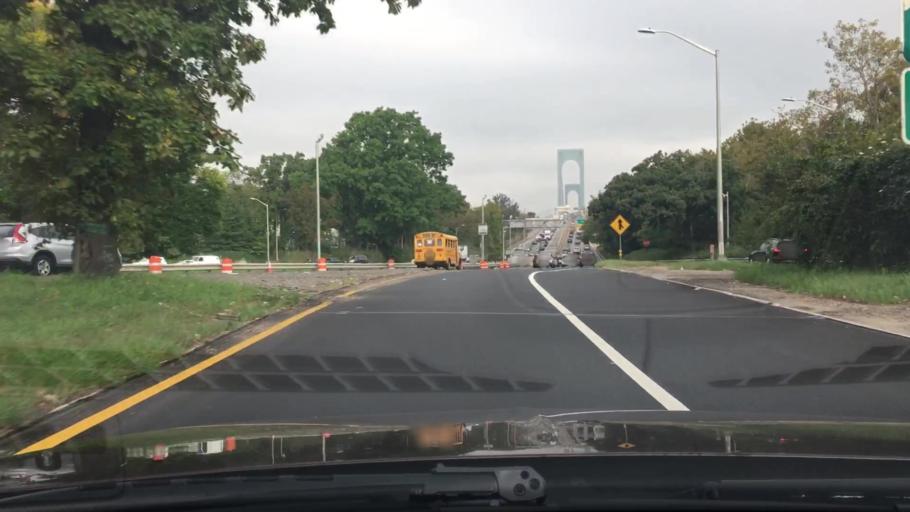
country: US
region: New York
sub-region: Bronx
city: The Bronx
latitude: 40.7907
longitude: -73.8224
